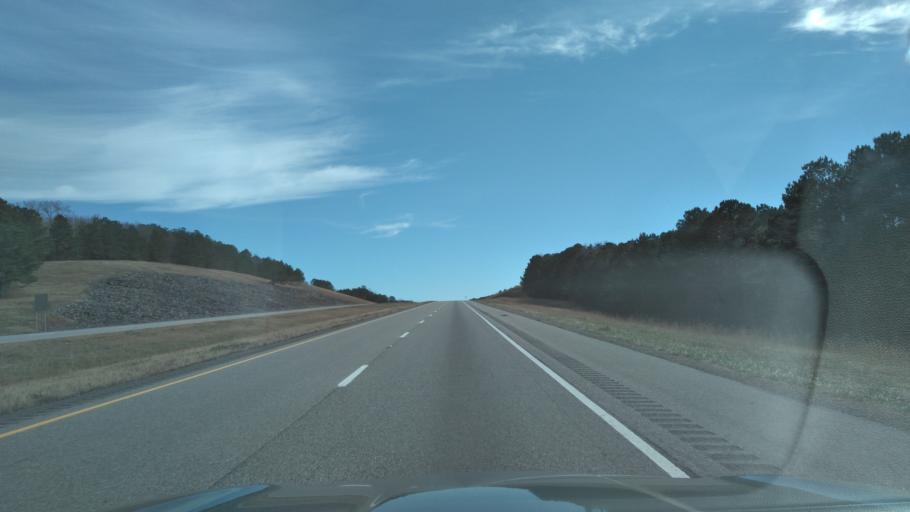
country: US
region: Alabama
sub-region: Marion County
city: Hamilton
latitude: 34.0586
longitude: -87.9475
